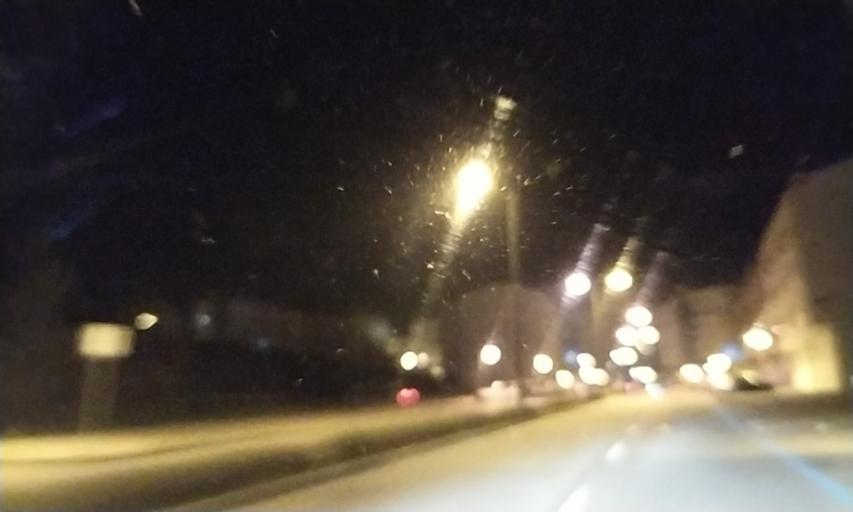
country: PT
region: Castelo Branco
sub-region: Concelho do Fundao
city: Fundao
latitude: 40.1419
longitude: -7.5041
